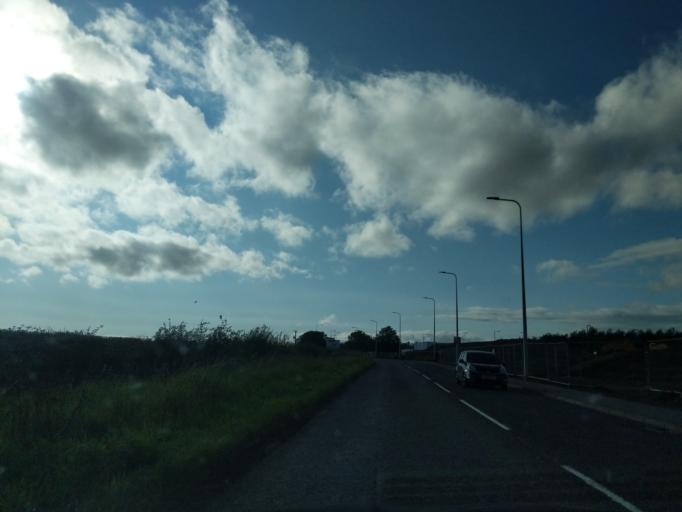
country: GB
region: Scotland
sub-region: East Lothian
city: Haddington
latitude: 55.9541
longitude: -2.8119
